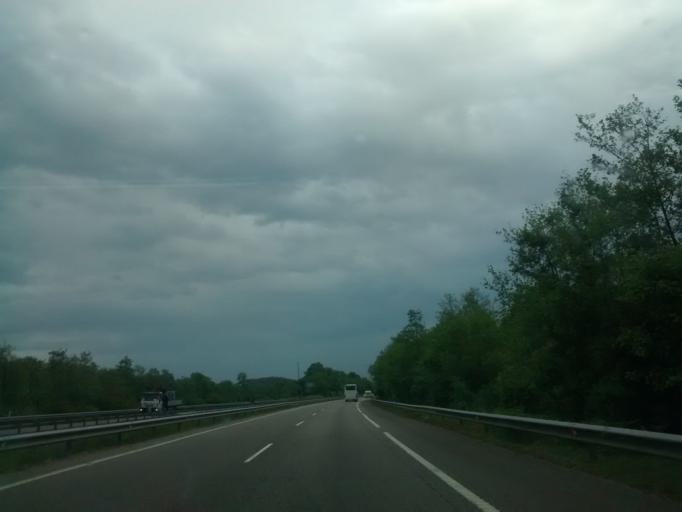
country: ES
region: Asturias
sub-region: Province of Asturias
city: Ribadesella
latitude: 43.4360
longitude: -4.9917
